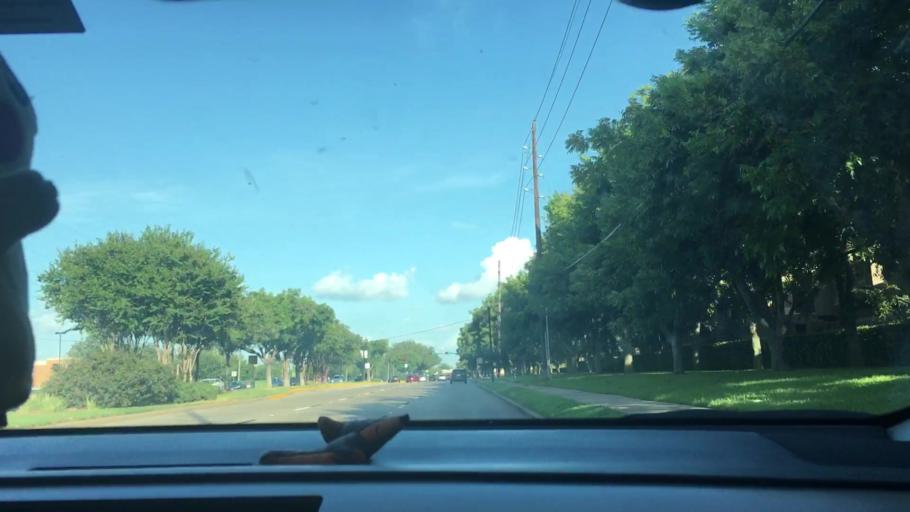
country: US
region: Texas
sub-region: Fort Bend County
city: Sugar Land
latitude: 29.6012
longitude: -95.6306
